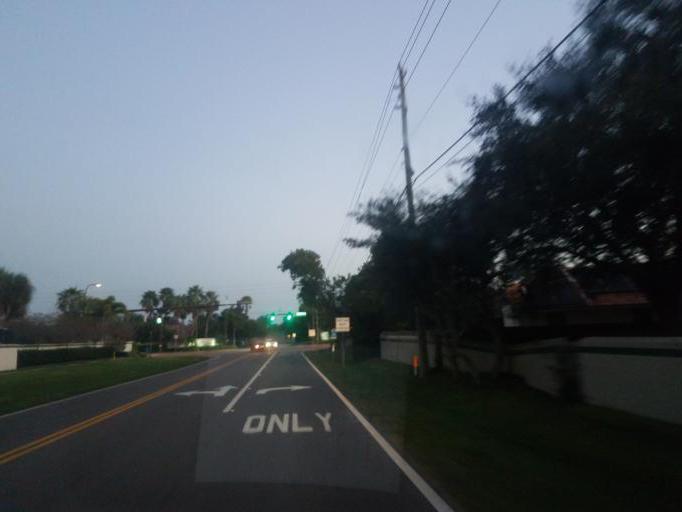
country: US
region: Florida
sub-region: Sarasota County
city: Lake Sarasota
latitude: 27.2831
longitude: -82.4563
